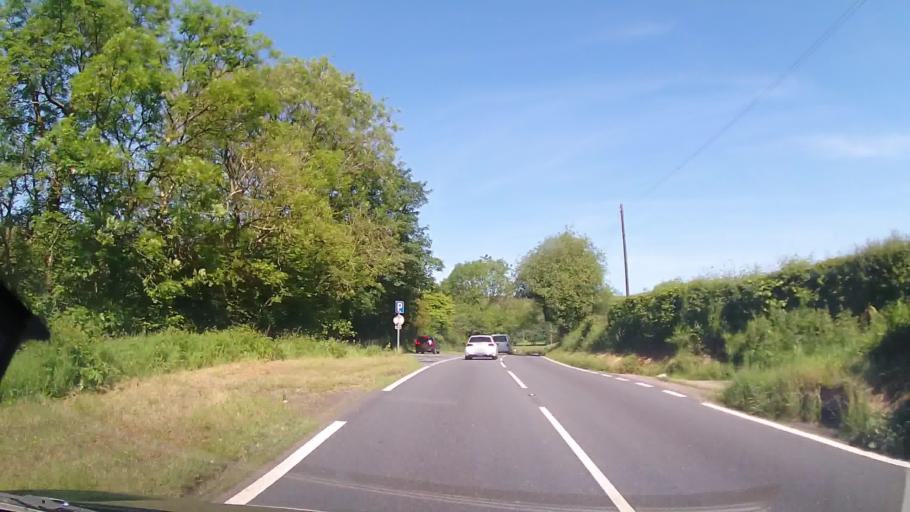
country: GB
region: Wales
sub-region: Sir Powys
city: Llangynog
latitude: 52.7075
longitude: -3.5607
